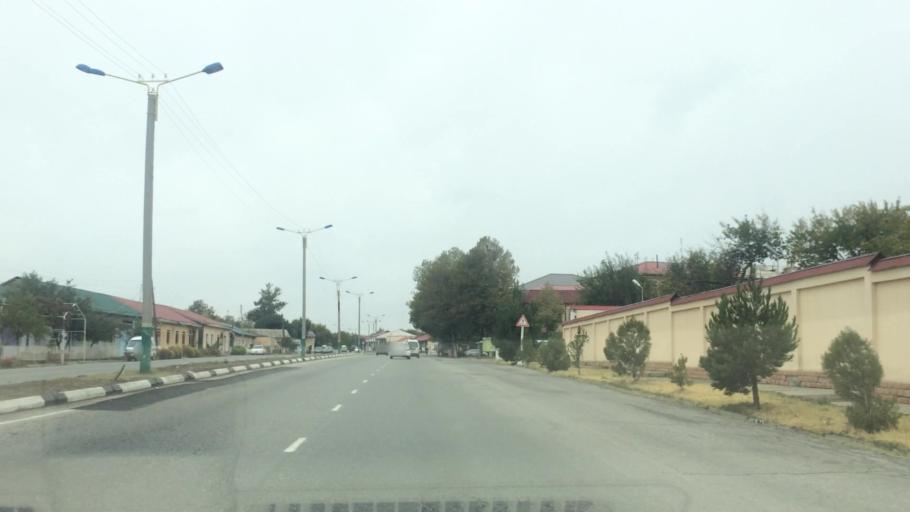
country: UZ
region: Samarqand
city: Bulung'ur
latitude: 39.7697
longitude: 67.2670
